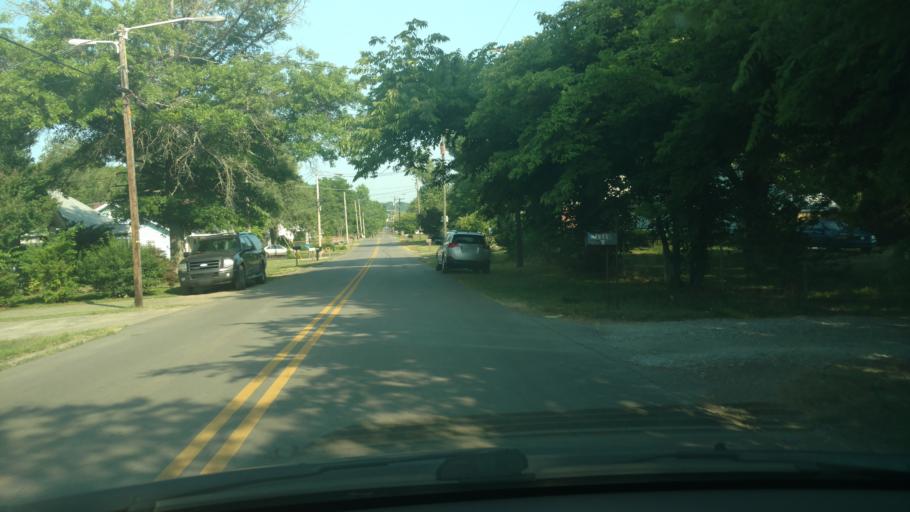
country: US
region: Tennessee
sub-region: Davidson County
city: Nashville
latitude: 36.2163
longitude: -86.7166
